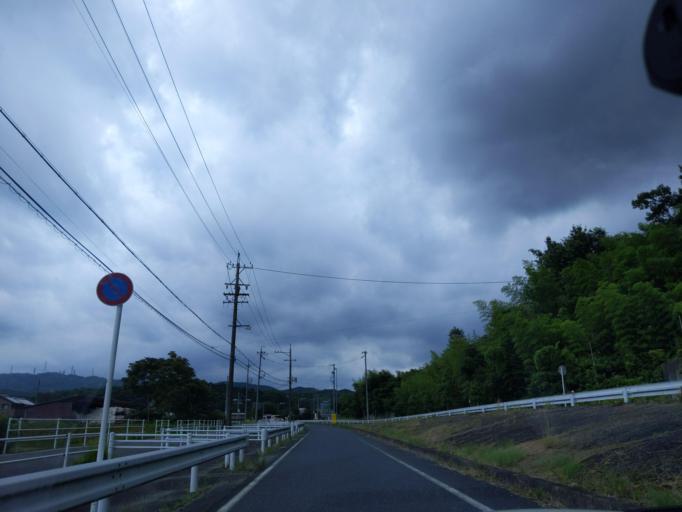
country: JP
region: Aichi
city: Seto
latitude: 35.1932
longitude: 137.1037
